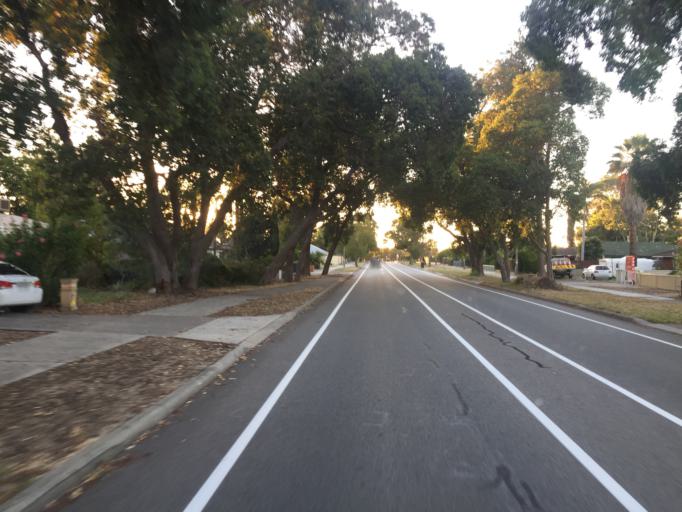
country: AU
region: Western Australia
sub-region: Gosnells
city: Maddington
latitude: -32.0328
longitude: 115.9853
